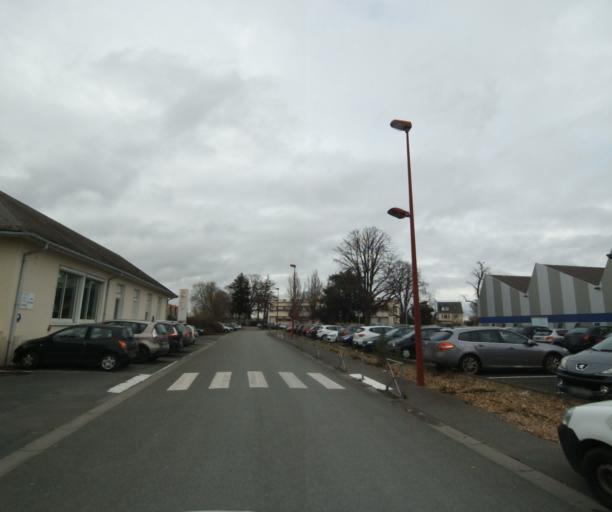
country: FR
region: Pays de la Loire
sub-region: Departement de la Sarthe
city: Le Mans
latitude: 47.9823
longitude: 0.2028
